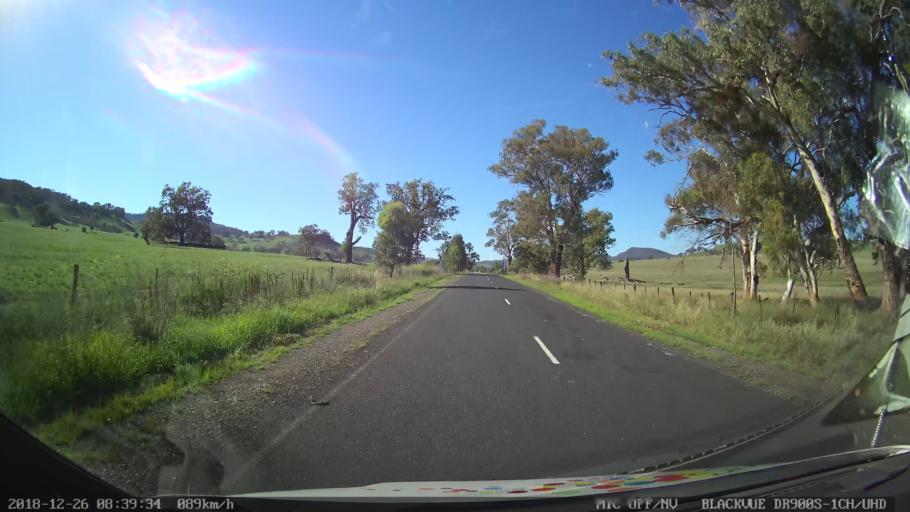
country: AU
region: New South Wales
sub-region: Mid-Western Regional
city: Kandos
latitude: -32.4552
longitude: 150.0756
